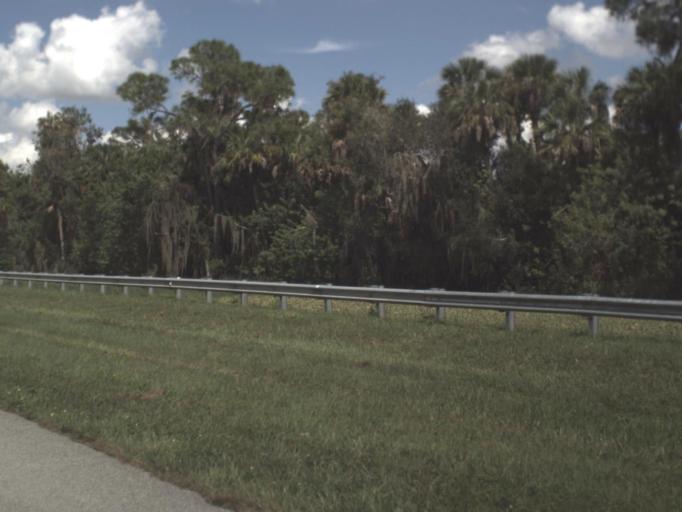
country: US
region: Florida
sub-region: Collier County
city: Immokalee
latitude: 26.2747
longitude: -81.3422
